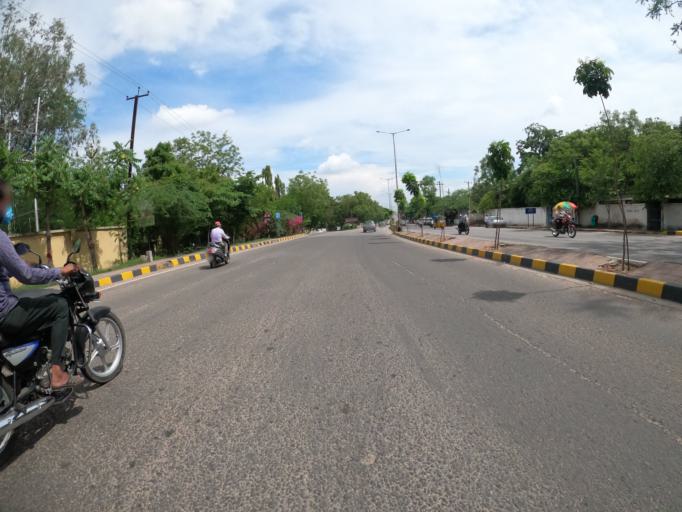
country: IN
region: Telangana
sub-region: Hyderabad
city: Hyderabad
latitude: 17.3832
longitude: 78.4225
